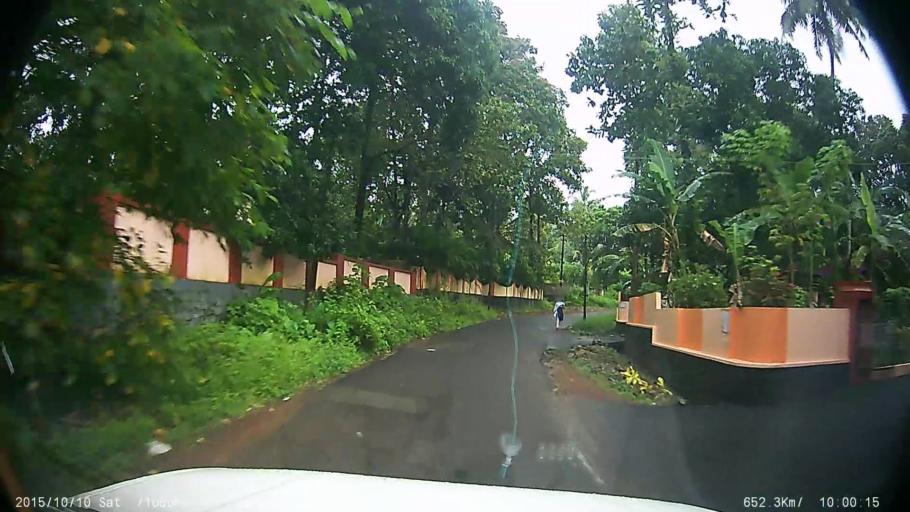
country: IN
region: Kerala
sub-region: Kottayam
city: Kottayam
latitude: 9.6413
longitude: 76.5346
